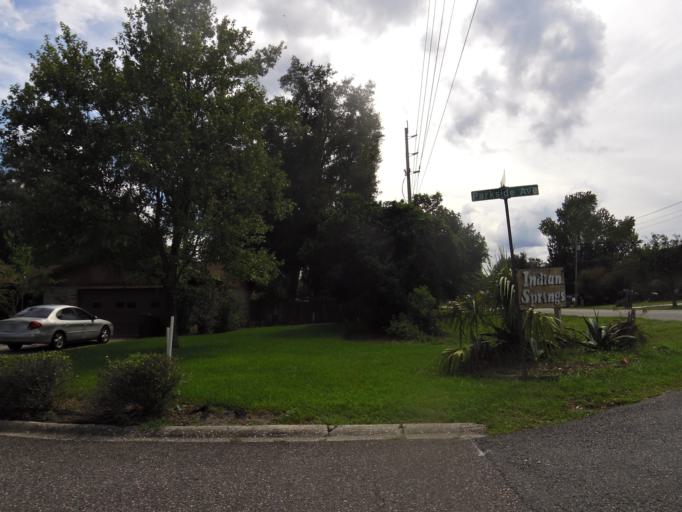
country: US
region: Florida
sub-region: Clay County
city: Lakeside
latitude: 30.1307
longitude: -81.7697
